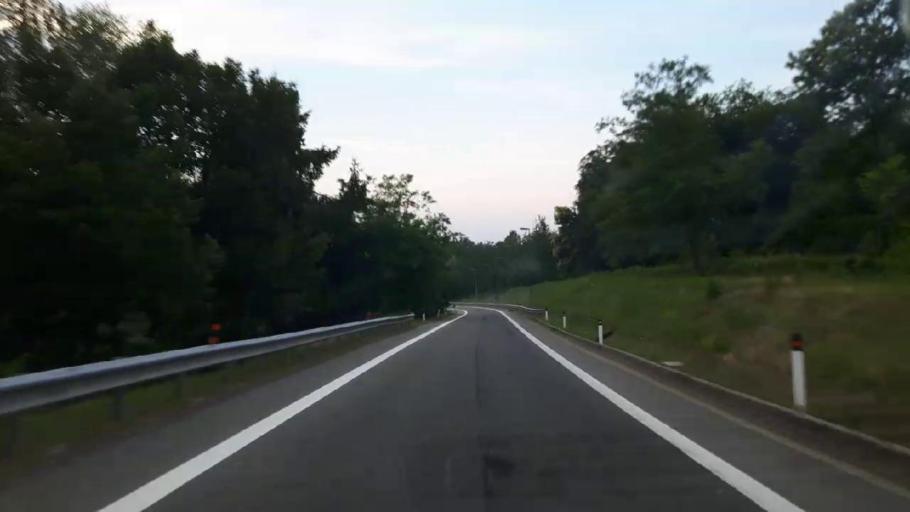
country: IT
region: Piedmont
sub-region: Provincia di Novara
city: Borgo Ticino
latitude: 45.7035
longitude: 8.6055
